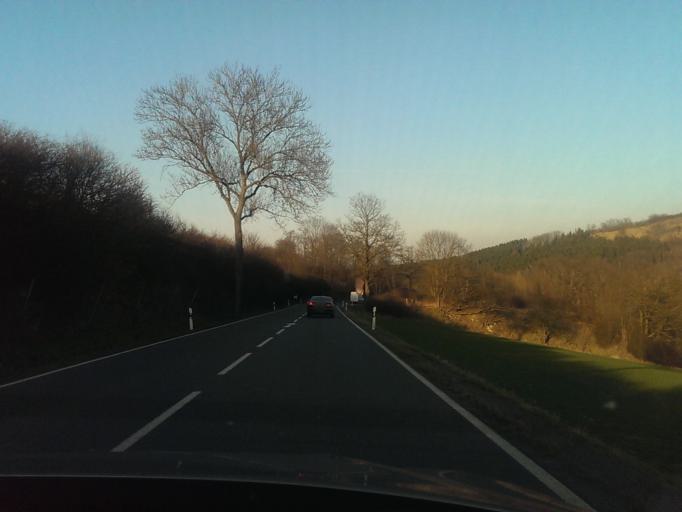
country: DE
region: Saxony
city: Weischlitz
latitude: 50.4149
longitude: 12.0555
